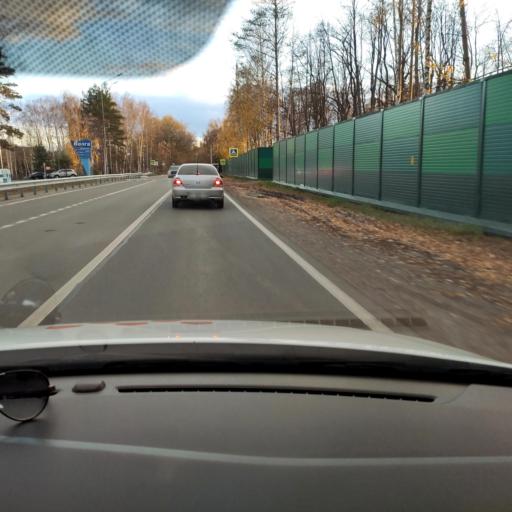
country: RU
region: Tatarstan
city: Verkhniy Uslon
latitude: 55.6260
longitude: 49.0140
